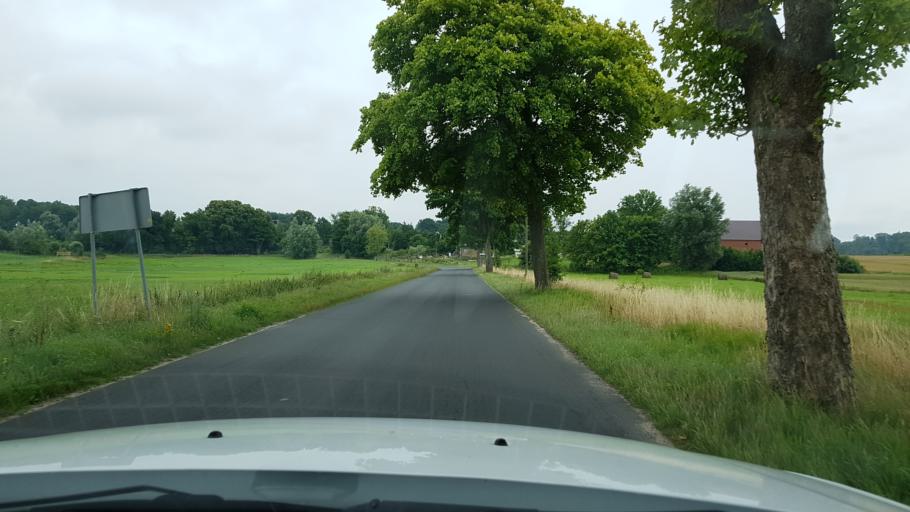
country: PL
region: West Pomeranian Voivodeship
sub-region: Powiat slawienski
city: Slawno
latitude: 54.4921
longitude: 16.5789
